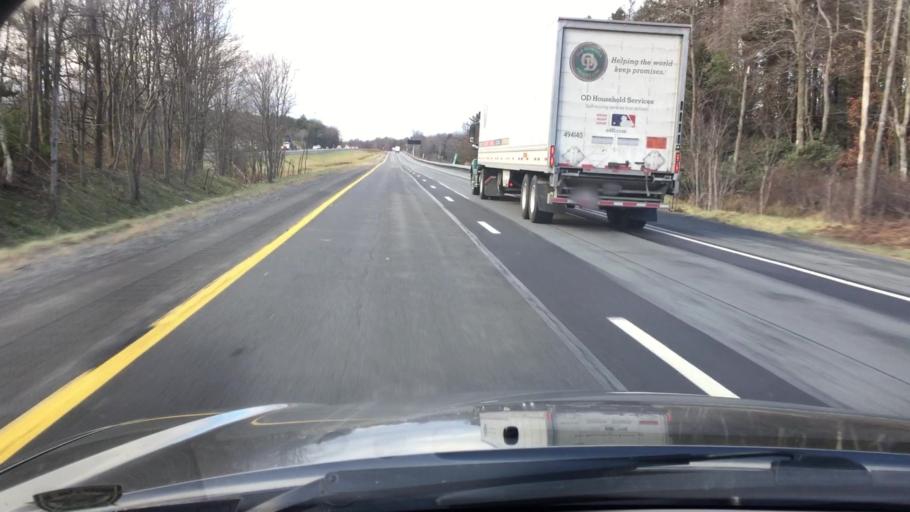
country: US
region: Pennsylvania
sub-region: Monroe County
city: Pocono Pines
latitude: 41.0743
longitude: -75.4996
